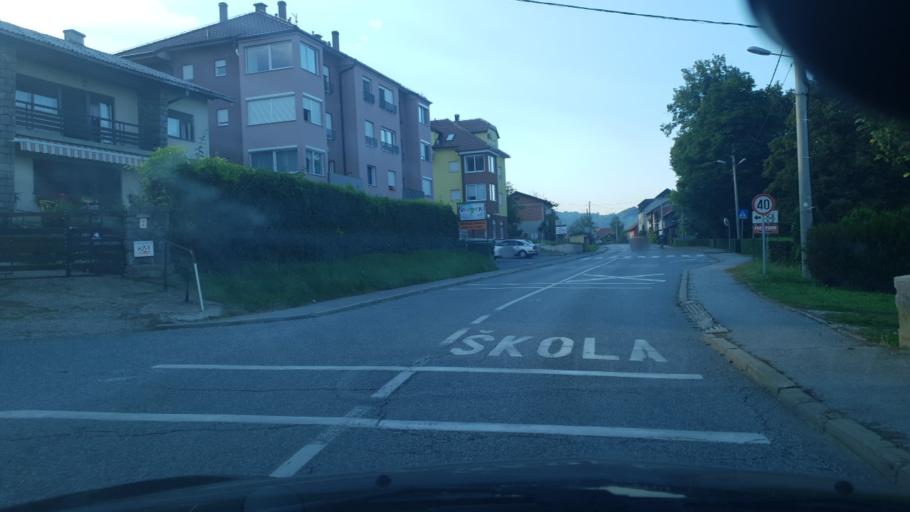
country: HR
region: Zagrebacka
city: Jakovlje
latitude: 45.9981
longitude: 15.8453
